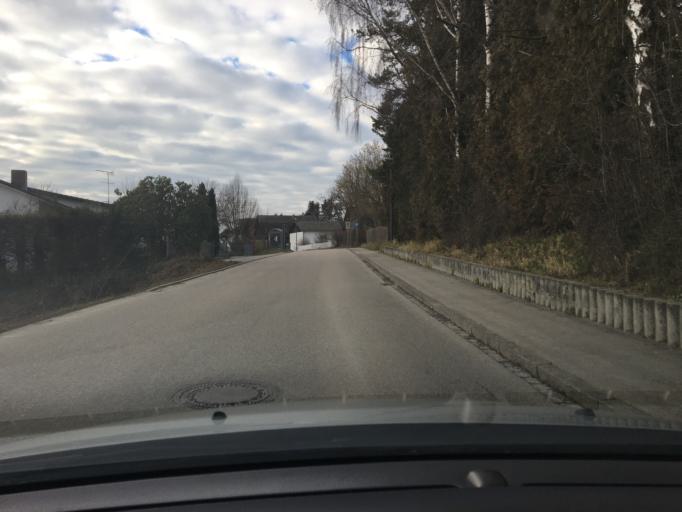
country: DE
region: Bavaria
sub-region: Lower Bavaria
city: Tiefenbach
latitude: 48.5055
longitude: 12.1331
